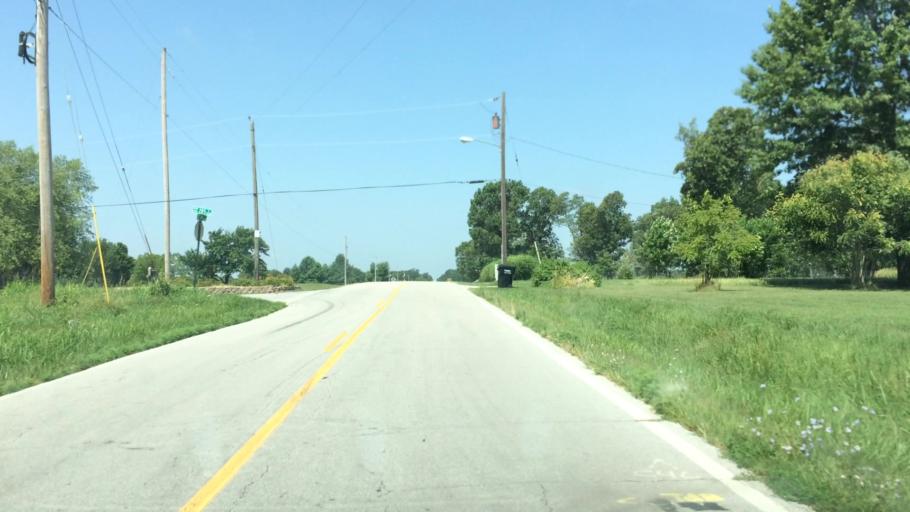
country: US
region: Missouri
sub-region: Greene County
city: Strafford
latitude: 37.2716
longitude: -93.1682
